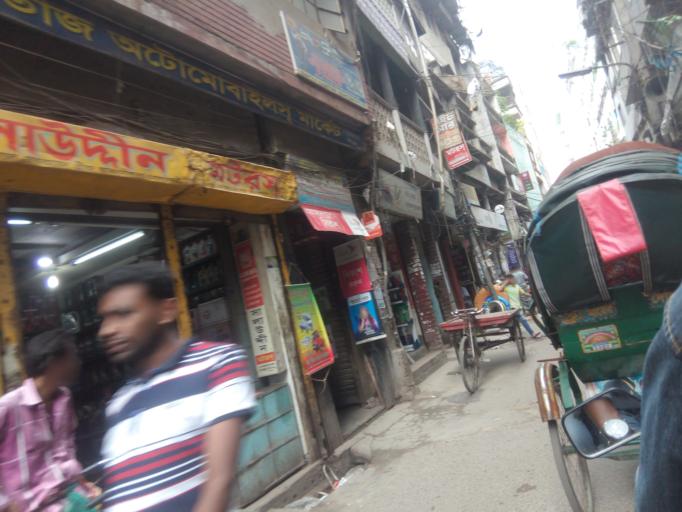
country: BD
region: Dhaka
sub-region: Dhaka
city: Dhaka
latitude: 23.7076
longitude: 90.4125
